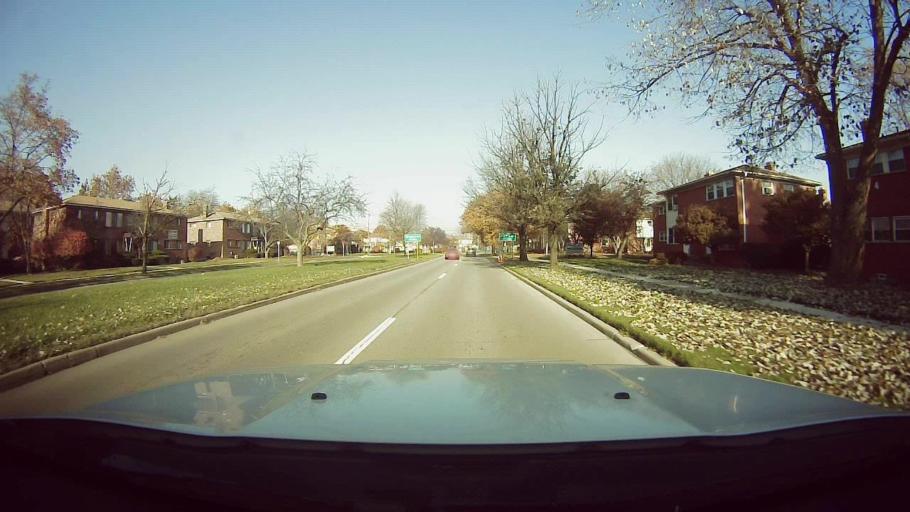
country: US
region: Michigan
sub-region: Oakland County
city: Berkley
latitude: 42.5132
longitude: -83.1861
